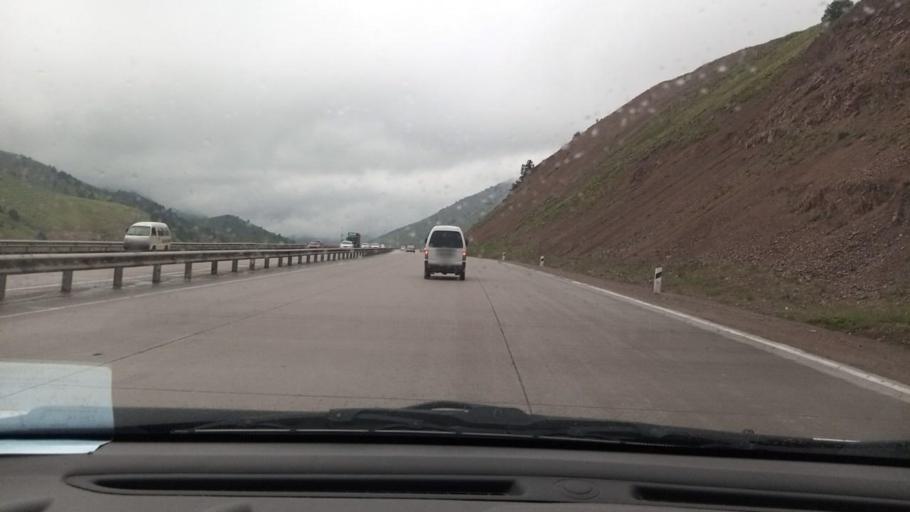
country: UZ
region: Toshkent
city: Angren
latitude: 41.1060
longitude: 70.5050
